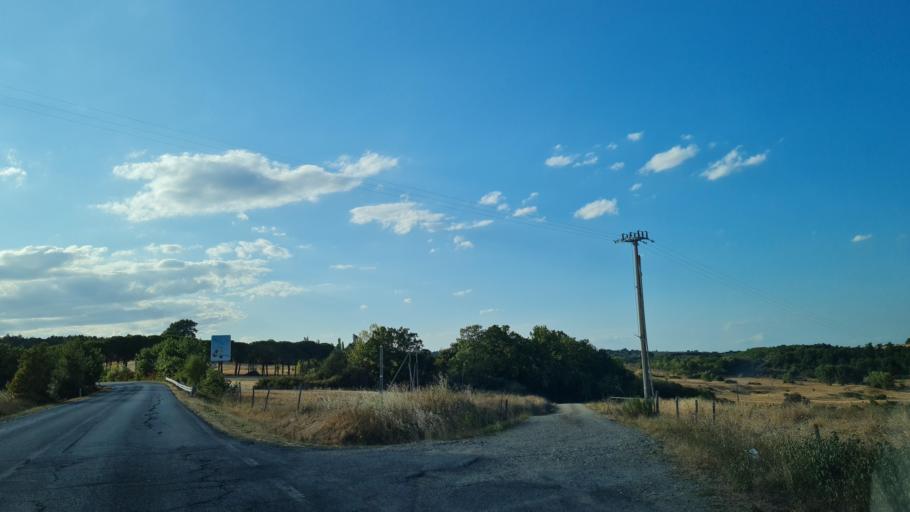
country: IT
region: Tuscany
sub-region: Provincia di Siena
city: Sarteano
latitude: 43.0313
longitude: 11.8532
